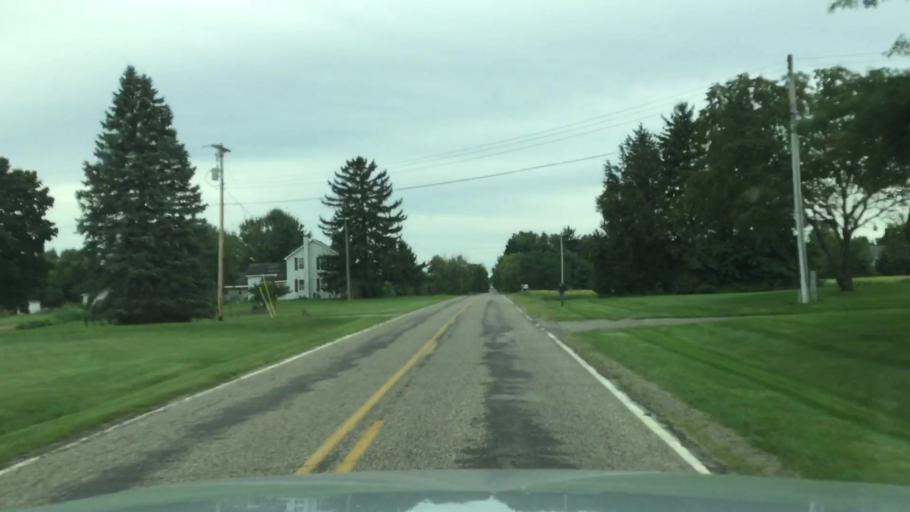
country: US
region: Michigan
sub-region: Shiawassee County
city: Durand
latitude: 42.8937
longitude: -84.0690
